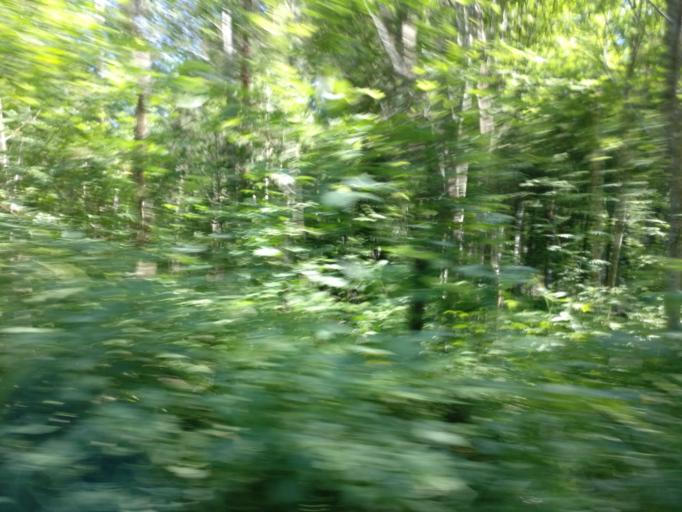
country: FI
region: Southern Savonia
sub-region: Savonlinna
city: Rantasalmi
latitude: 62.1691
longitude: 28.2480
